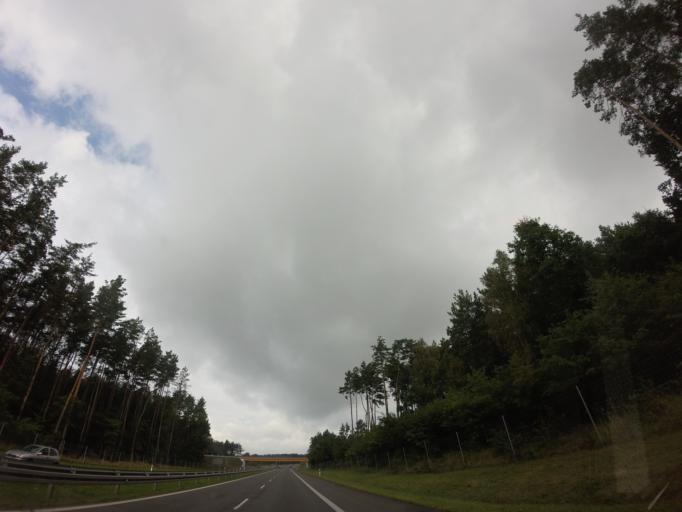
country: PL
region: West Pomeranian Voivodeship
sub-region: Powiat goleniowski
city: Goleniow
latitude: 53.6099
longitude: 14.8200
